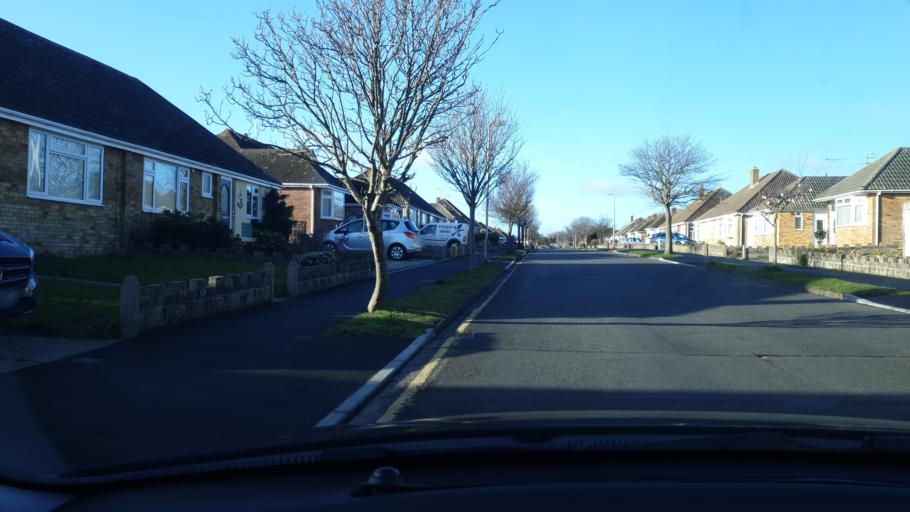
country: GB
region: England
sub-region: Essex
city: Walton-on-the-Naze
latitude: 51.8427
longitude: 1.2615
